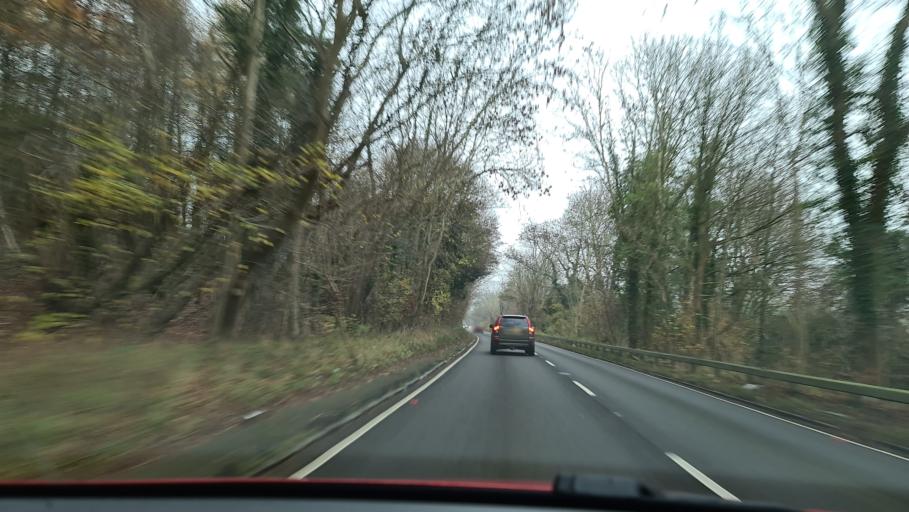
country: GB
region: England
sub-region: Buckinghamshire
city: Stokenchurch
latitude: 51.6448
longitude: -0.8479
